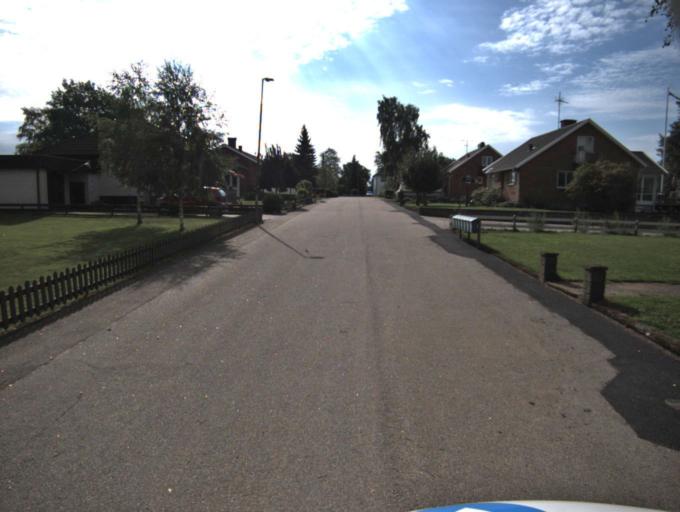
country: SE
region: Vaestra Goetaland
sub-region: Falkopings Kommun
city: Falkoeping
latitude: 57.9850
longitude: 13.5371
